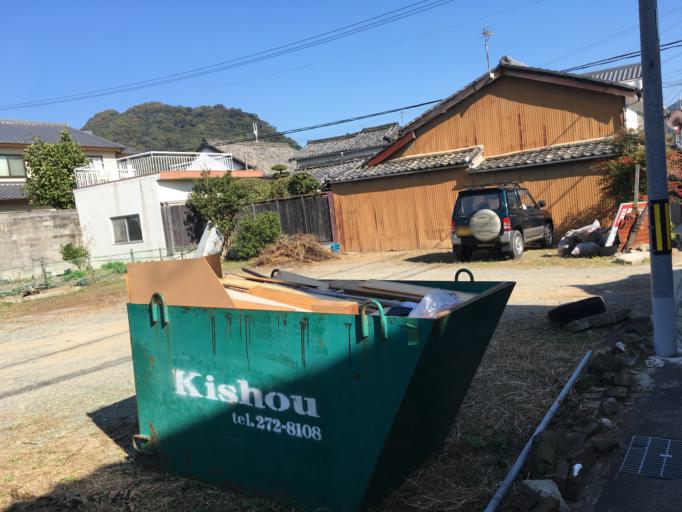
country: JP
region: Hyogo
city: Tatsunocho-tominaga
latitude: 34.8633
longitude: 134.5442
